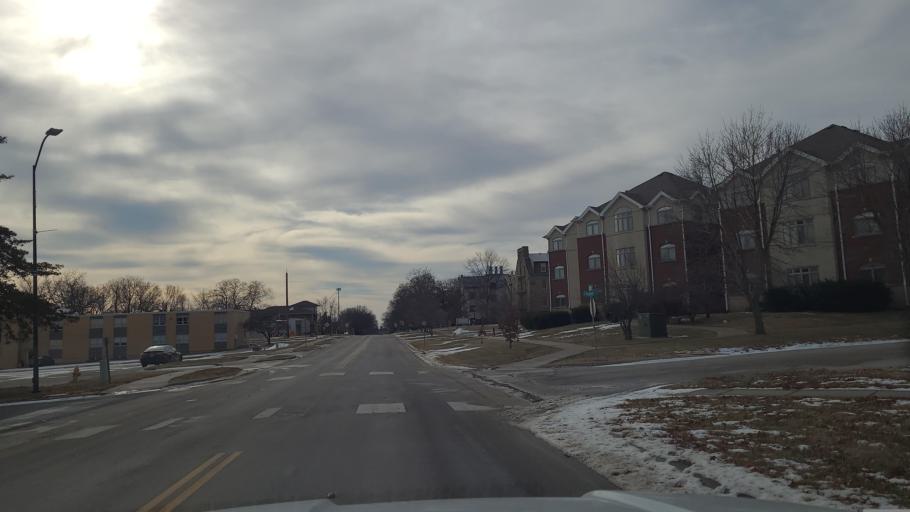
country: US
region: Kansas
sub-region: Douglas County
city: Baldwin City
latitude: 38.7804
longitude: -95.1862
